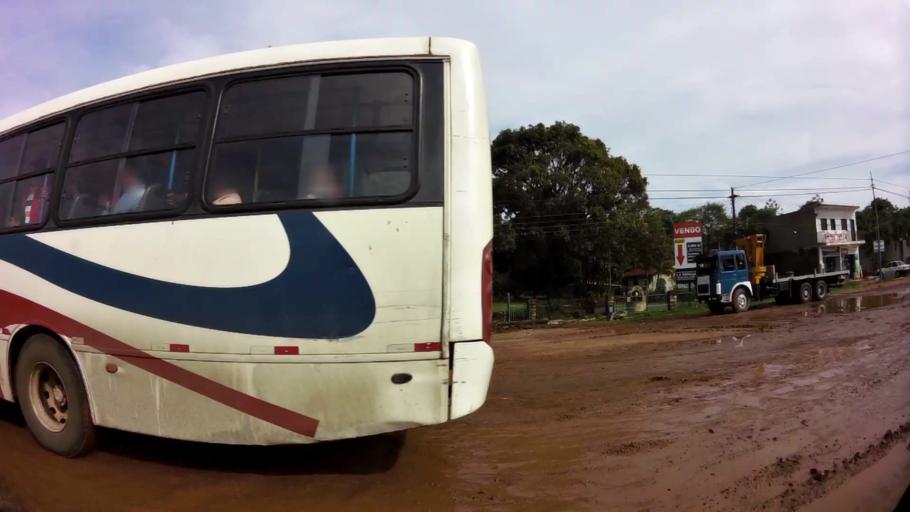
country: PY
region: Central
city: Limpio
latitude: -25.1746
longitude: -57.4837
